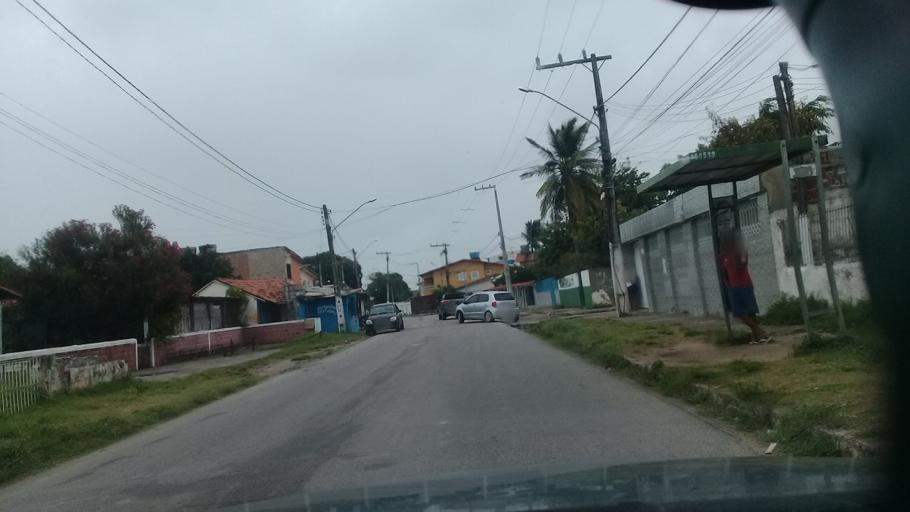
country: BR
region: Pernambuco
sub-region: Itamaraca
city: Itamaraca
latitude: -7.7410
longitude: -34.8248
